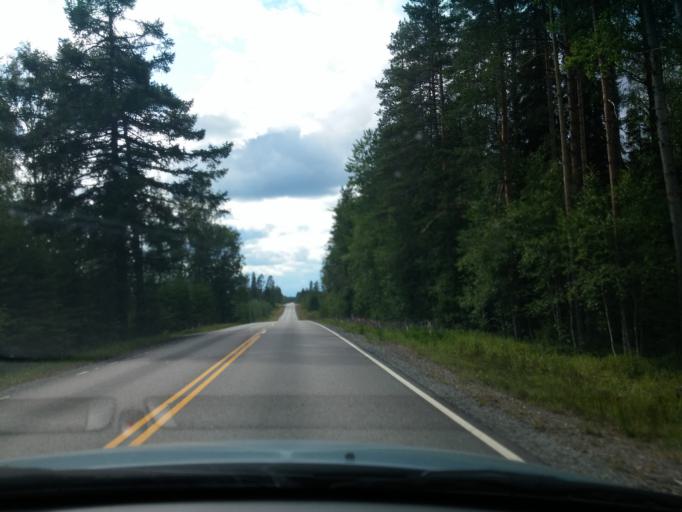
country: FI
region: Central Finland
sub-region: Saarijaervi-Viitasaari
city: Pylkoenmaeki
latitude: 62.6137
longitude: 24.7180
